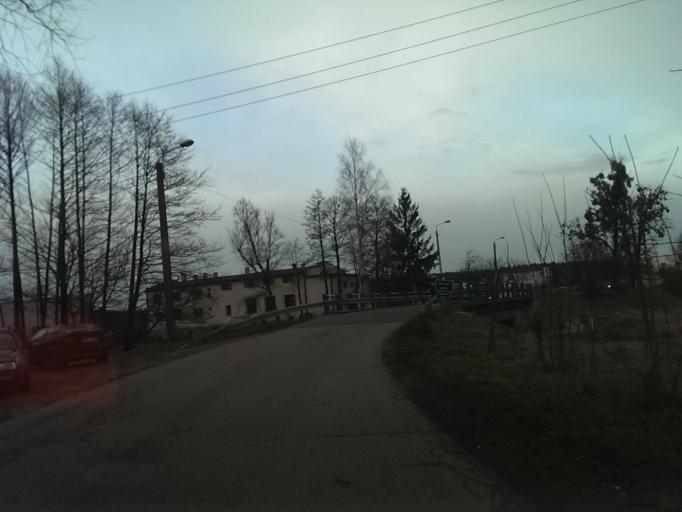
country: PL
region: Kujawsko-Pomorskie
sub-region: Powiat nakielski
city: Szubin
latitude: 53.0821
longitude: 17.7317
